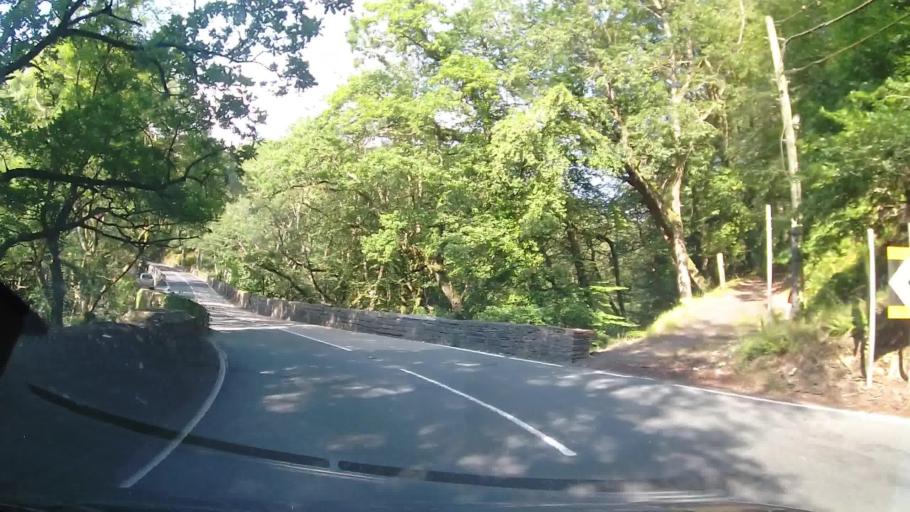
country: GB
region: Wales
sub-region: Gwynedd
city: Ffestiniog
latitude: 52.9551
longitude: -3.9558
